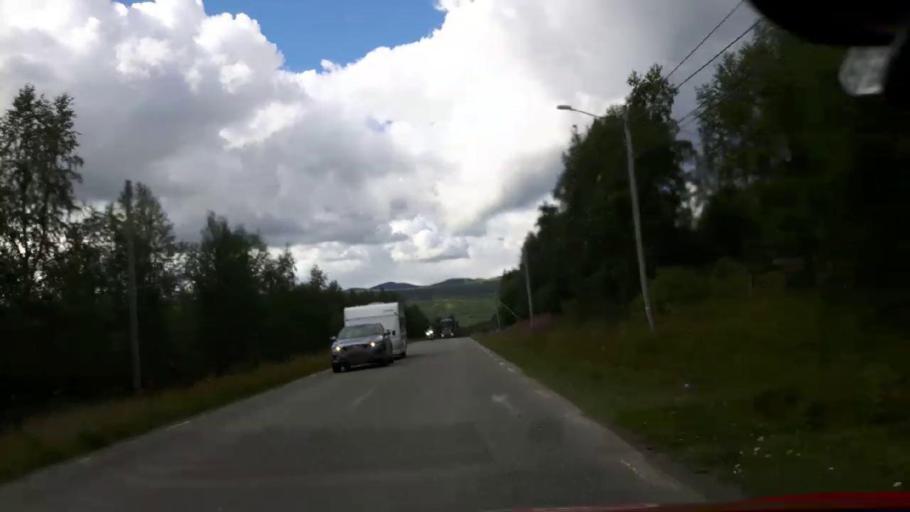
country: NO
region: Nordland
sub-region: Hattfjelldal
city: Hattfjelldal
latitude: 65.0583
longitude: 14.7859
